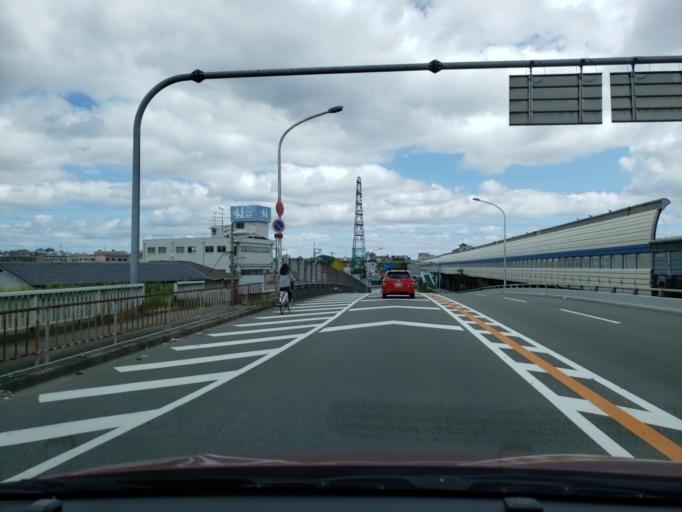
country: JP
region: Osaka
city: Toyonaka
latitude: 34.7580
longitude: 135.4791
